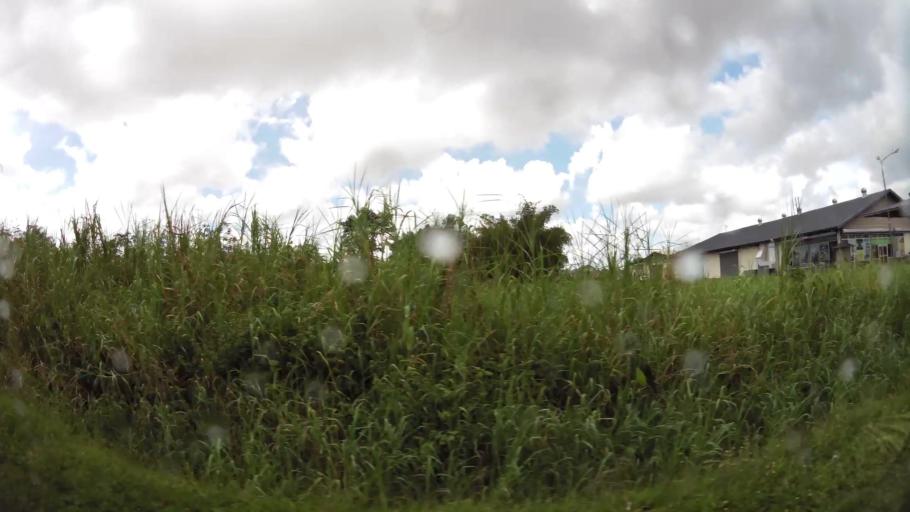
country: SR
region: Paramaribo
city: Paramaribo
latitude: 5.8333
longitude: -55.2142
